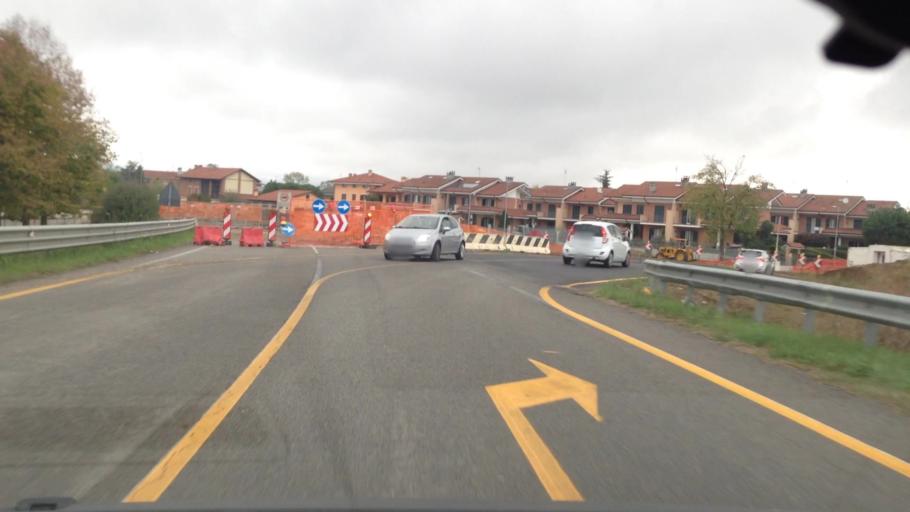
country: IT
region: Piedmont
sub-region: Provincia di Torino
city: Riva Presso Chieri
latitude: 44.9866
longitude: 7.8764
